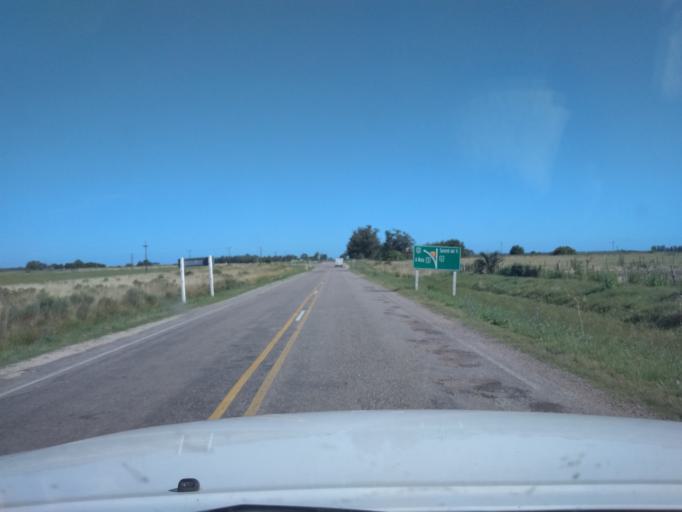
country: UY
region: Canelones
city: San Ramon
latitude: -34.2059
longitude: -55.9318
